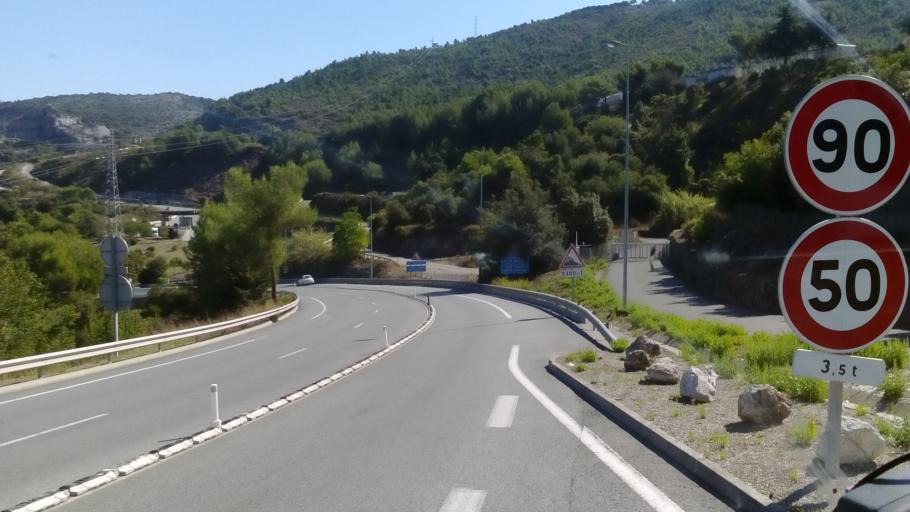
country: FR
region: Provence-Alpes-Cote d'Azur
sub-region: Departement des Alpes-Maritimes
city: La Turbie
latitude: 43.7447
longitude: 7.3741
